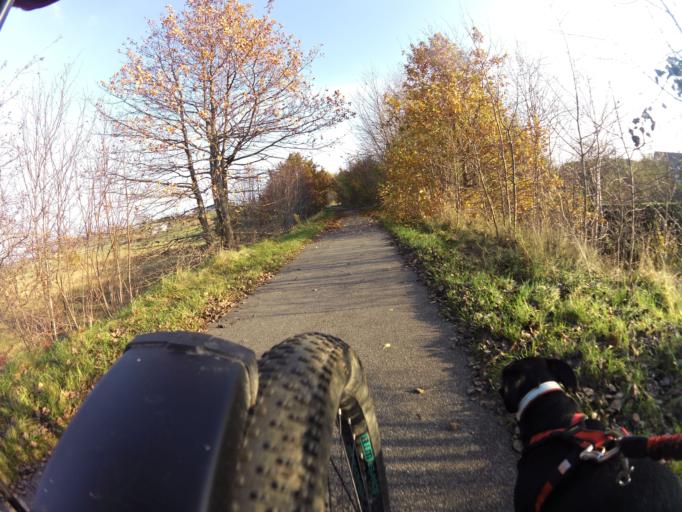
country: PL
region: Pomeranian Voivodeship
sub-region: Powiat pucki
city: Krokowa
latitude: 54.7816
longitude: 18.1663
